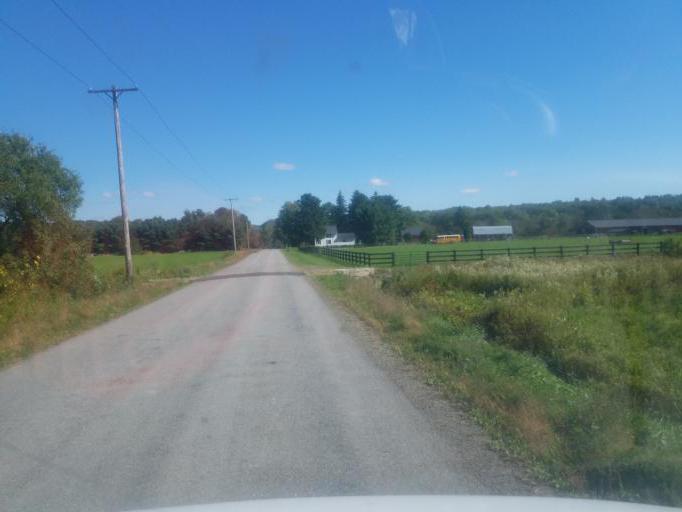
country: US
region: New York
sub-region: Allegany County
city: Friendship
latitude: 42.3148
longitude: -78.1127
